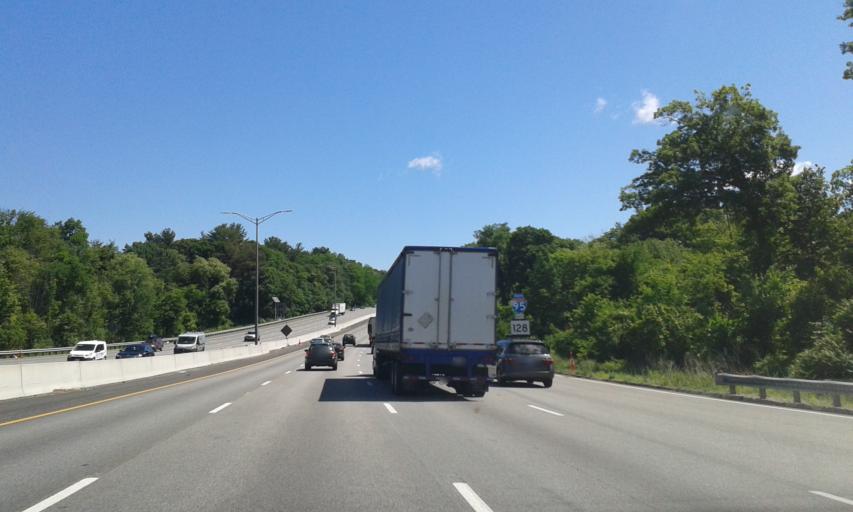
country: US
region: Massachusetts
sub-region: Middlesex County
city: Burlington
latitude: 42.4912
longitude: -71.1876
